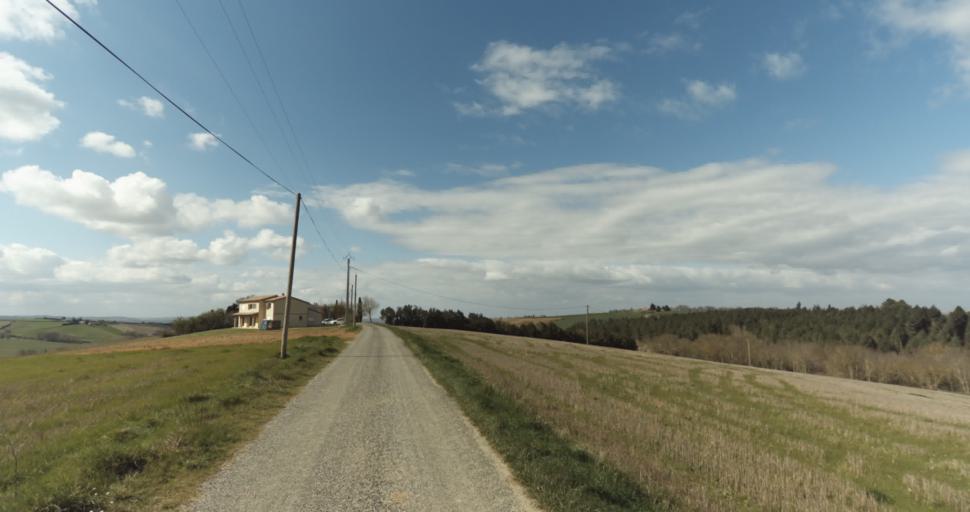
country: FR
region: Midi-Pyrenees
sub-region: Departement de la Haute-Garonne
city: Auterive
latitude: 43.3682
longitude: 1.5061
